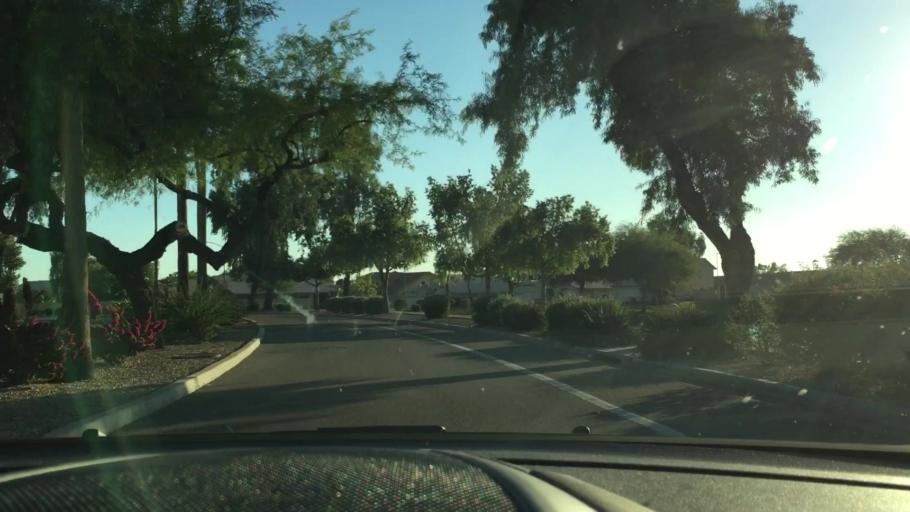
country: US
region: Arizona
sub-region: Maricopa County
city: Sun City
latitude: 33.6594
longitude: -112.2307
